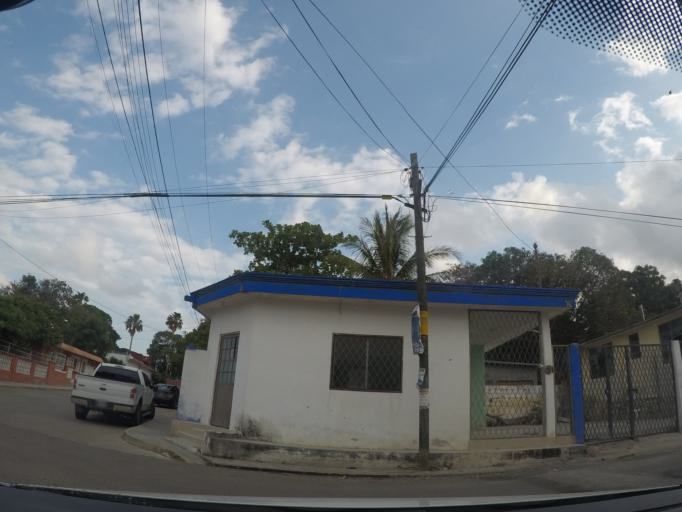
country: MX
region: Oaxaca
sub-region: Salina Cruz
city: Salina Cruz
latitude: 16.2073
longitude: -95.2072
